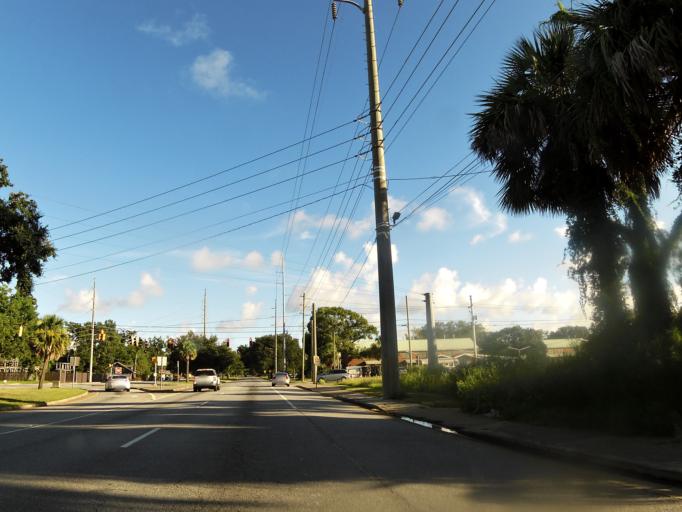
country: US
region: Georgia
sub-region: Glynn County
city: Brunswick
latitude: 31.1608
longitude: -81.4917
